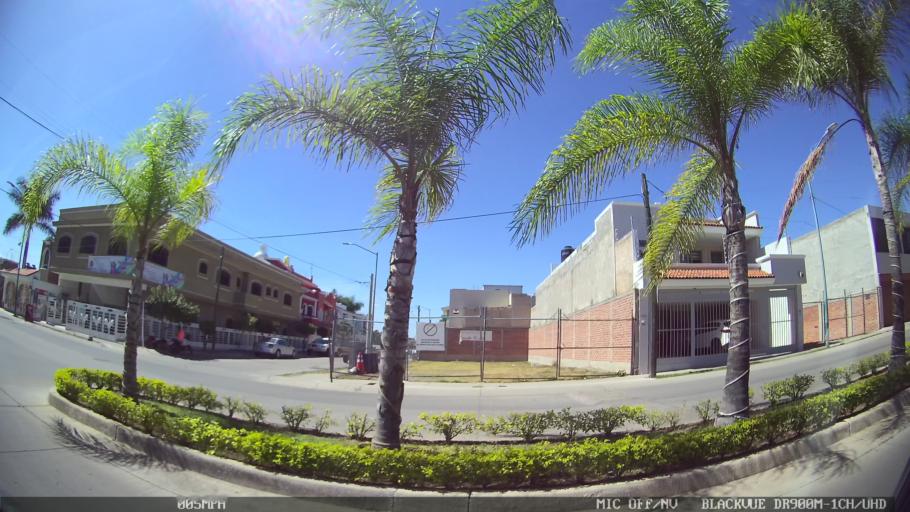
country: MX
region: Jalisco
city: Tlaquepaque
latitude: 20.6470
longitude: -103.2829
